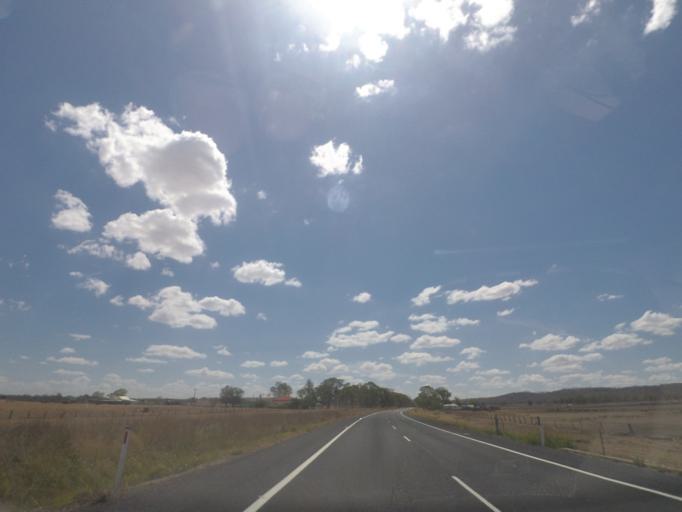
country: AU
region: Queensland
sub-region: Southern Downs
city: Warwick
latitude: -28.1781
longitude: 151.7743
